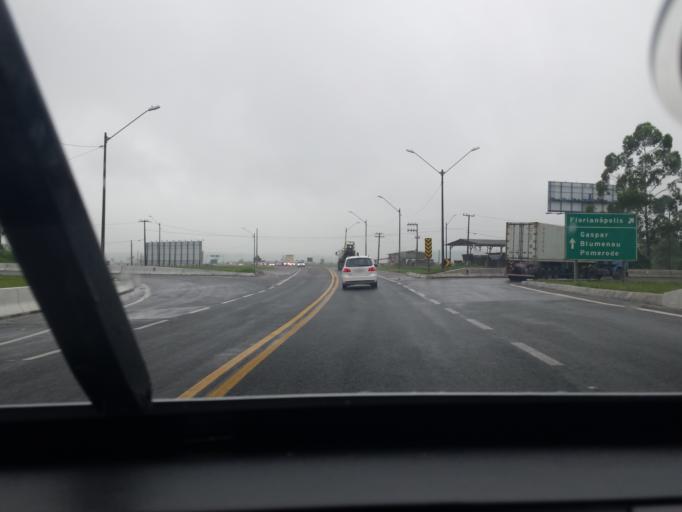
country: BR
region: Santa Catarina
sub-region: Navegantes
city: Navegantes
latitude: -26.8402
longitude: -48.7166
